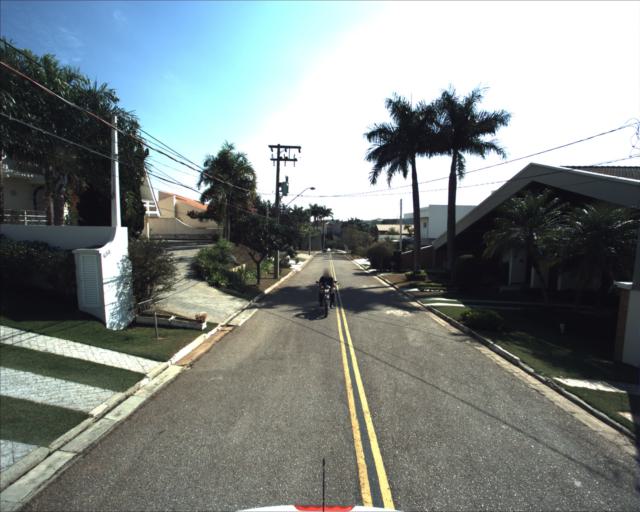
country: BR
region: Sao Paulo
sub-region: Sorocaba
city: Sorocaba
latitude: -23.4938
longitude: -47.4234
